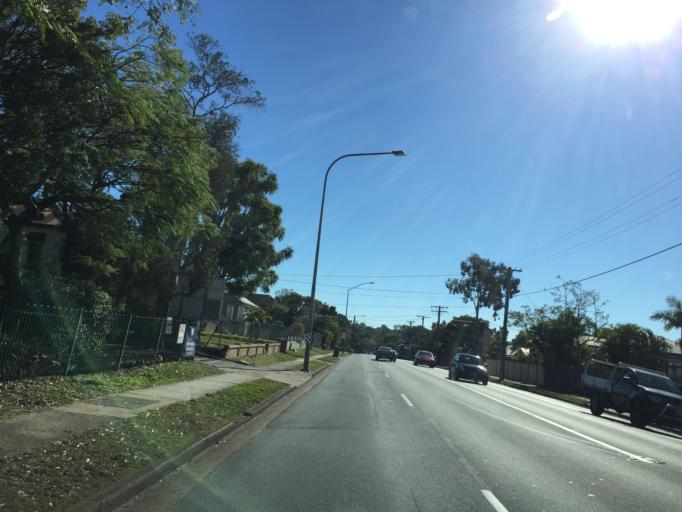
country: AU
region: Queensland
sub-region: Brisbane
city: Everton Park
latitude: -27.4154
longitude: 152.9921
